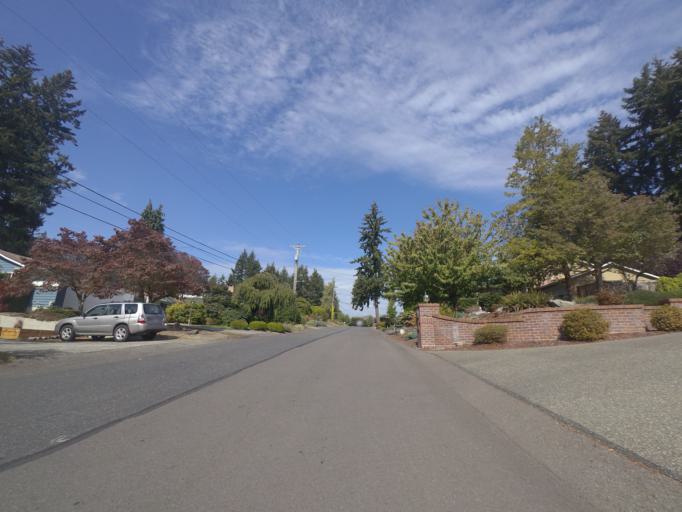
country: US
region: Washington
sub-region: Pierce County
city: Fircrest
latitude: 47.2158
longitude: -122.5289
